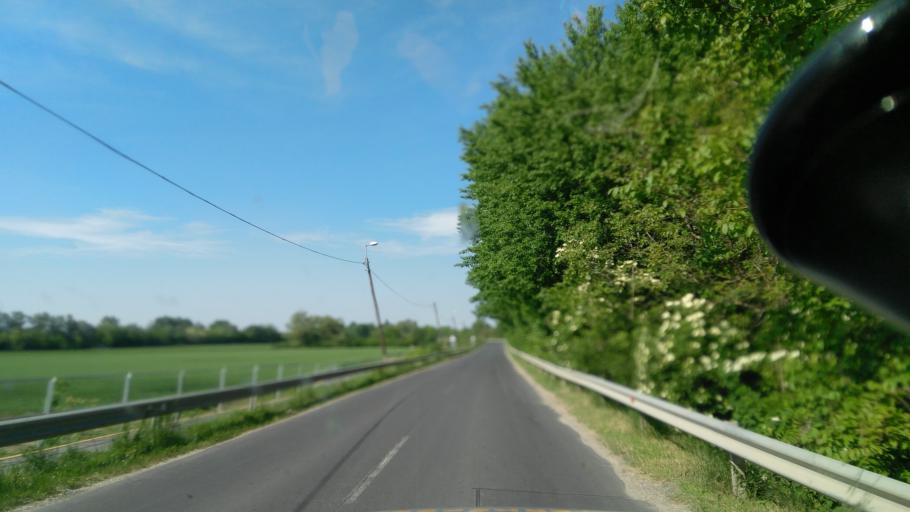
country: HU
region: Bekes
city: Gyula
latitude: 46.6654
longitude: 21.2978
